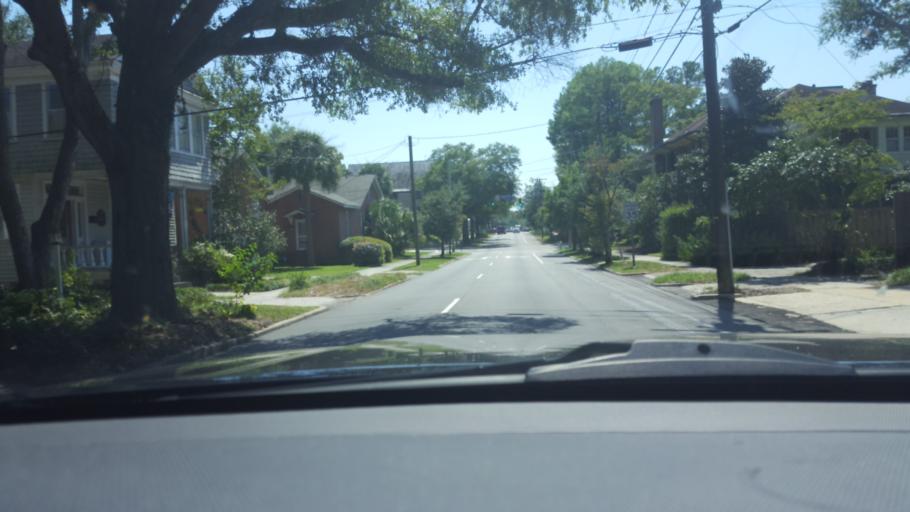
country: US
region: North Carolina
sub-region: New Hanover County
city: Wilmington
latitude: 34.2388
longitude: -77.9292
